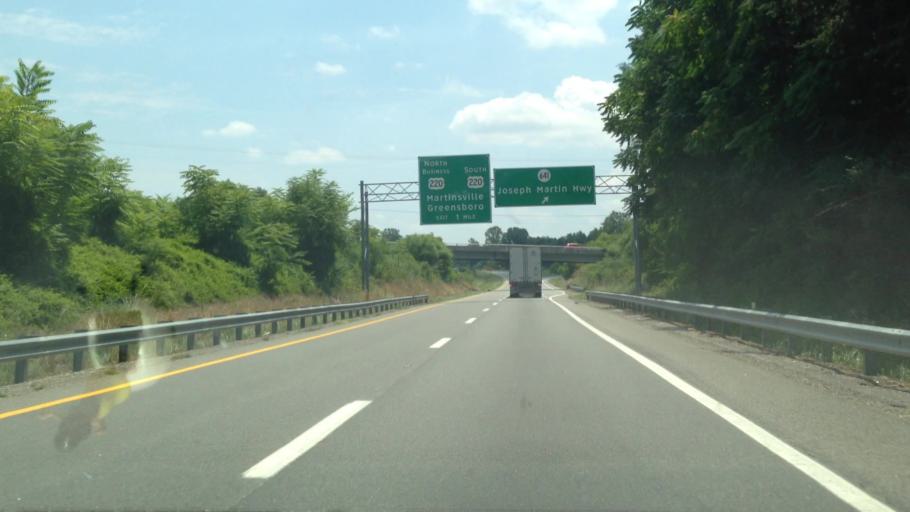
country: US
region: Virginia
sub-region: City of Martinsville
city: Martinsville
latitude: 36.6300
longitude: -79.8824
